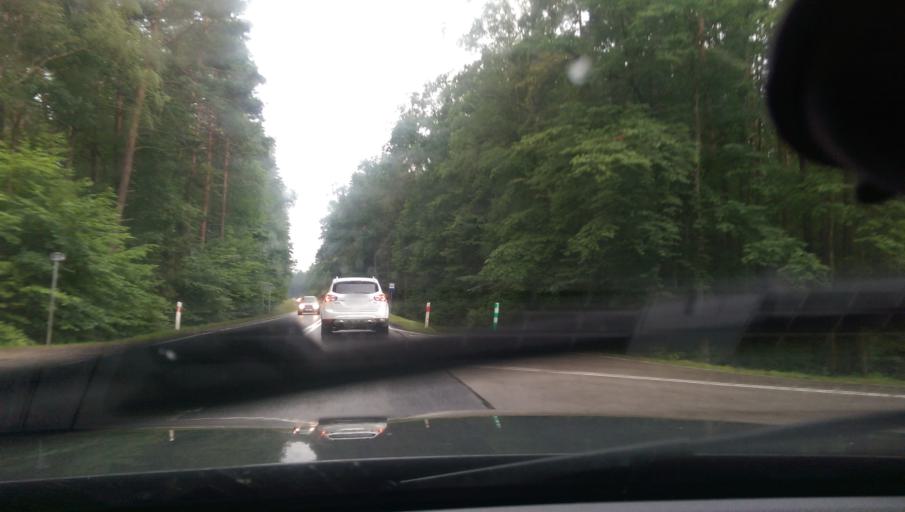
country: PL
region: Warmian-Masurian Voivodeship
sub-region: Powiat szczycienski
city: Szczytno
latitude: 53.5242
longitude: 20.9776
